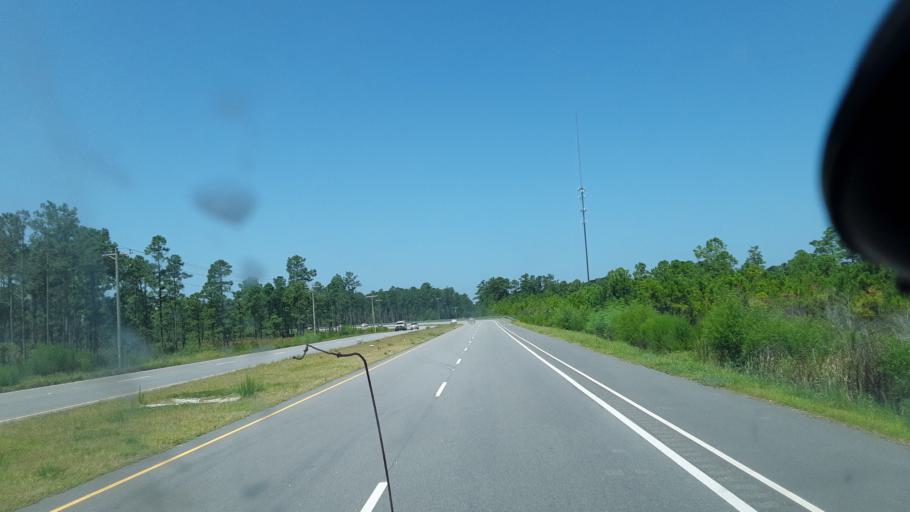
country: US
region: South Carolina
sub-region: Horry County
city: Forestbrook
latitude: 33.8152
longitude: -78.9028
